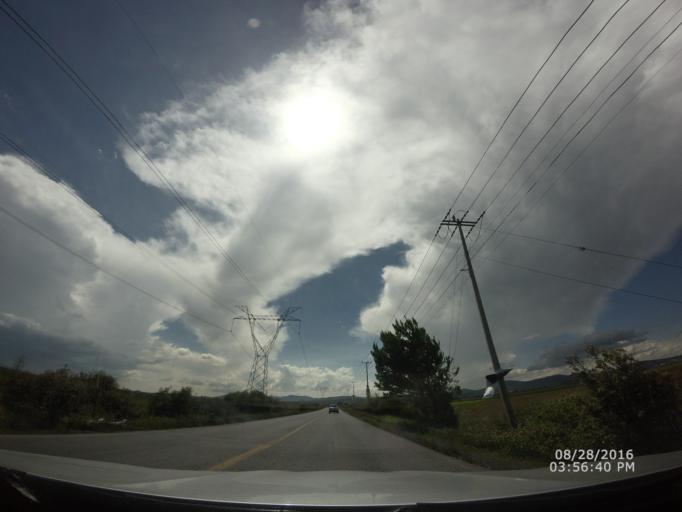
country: MX
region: Hidalgo
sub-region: Mineral de la Reforma
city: Los Tuzos
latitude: 20.0358
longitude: -98.7584
